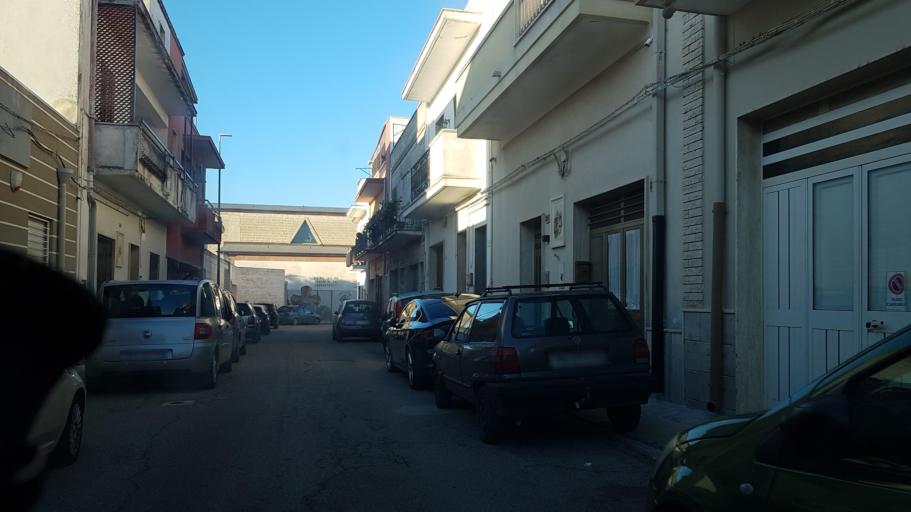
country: IT
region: Apulia
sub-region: Provincia di Brindisi
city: Latiano
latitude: 40.5501
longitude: 17.7209
